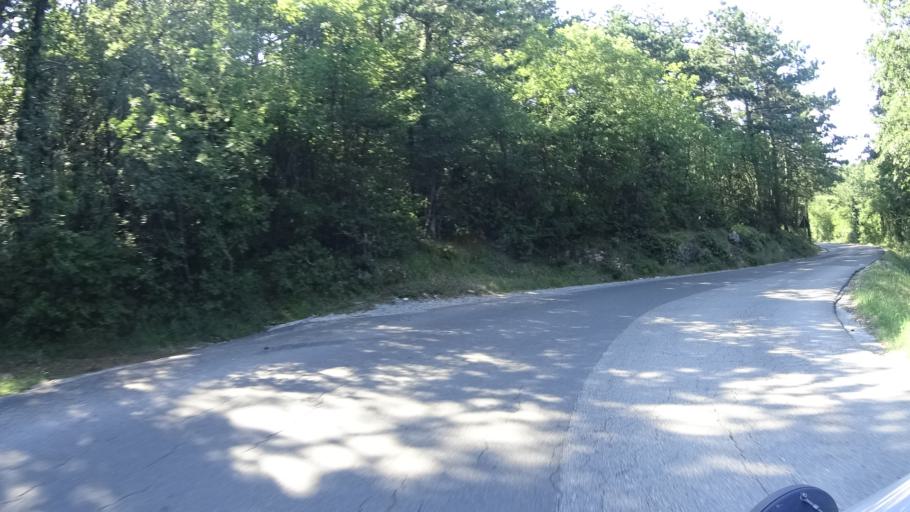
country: HR
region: Istarska
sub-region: Grad Labin
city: Labin
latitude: 45.0638
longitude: 14.1259
